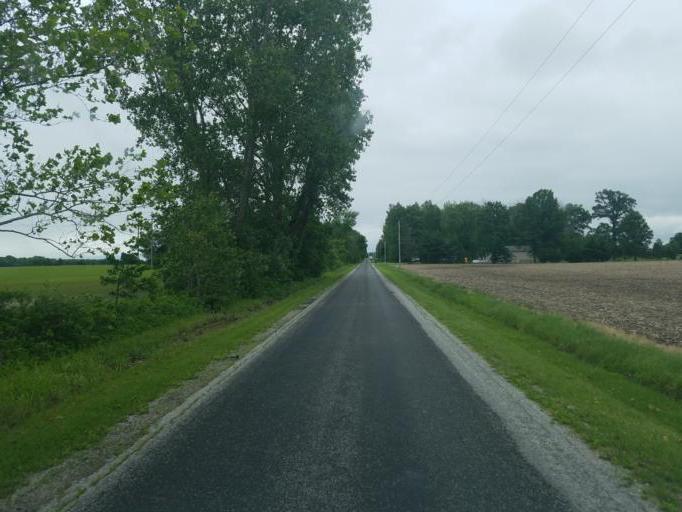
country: US
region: Ohio
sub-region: Marion County
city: Marion
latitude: 40.5056
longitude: -83.0408
